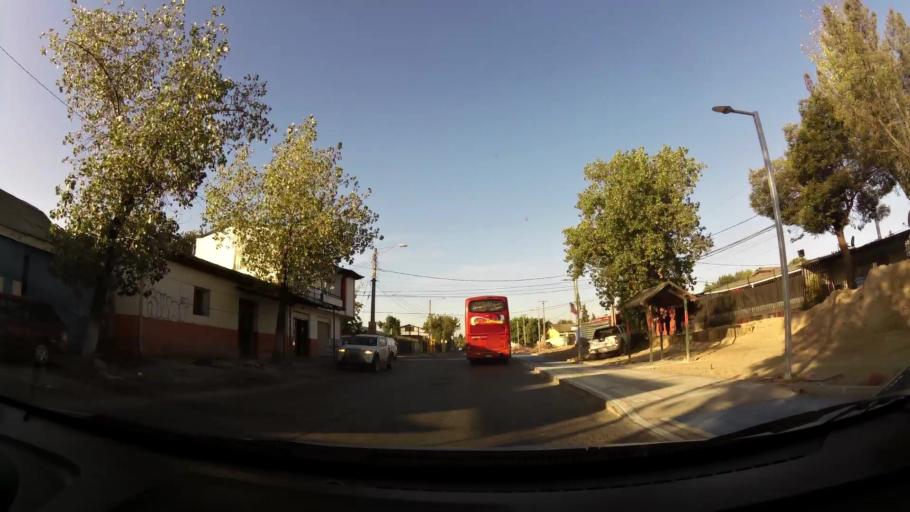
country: CL
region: Maule
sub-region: Provincia de Talca
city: Talca
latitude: -35.4335
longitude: -71.6416
